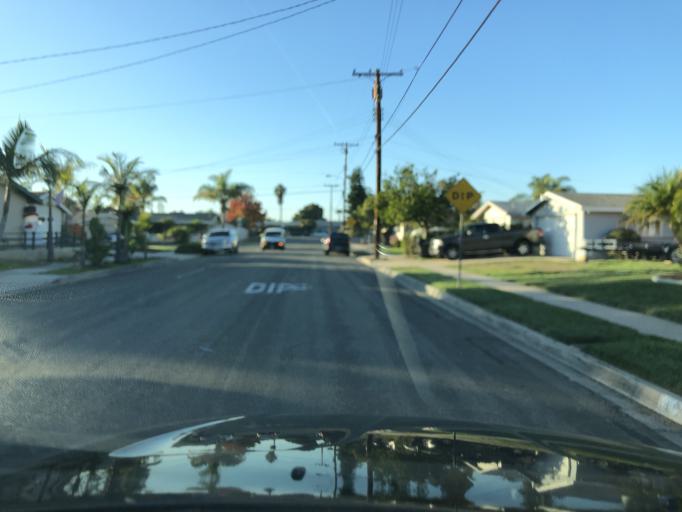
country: US
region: California
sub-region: San Diego County
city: La Jolla
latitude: 32.8212
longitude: -117.1939
